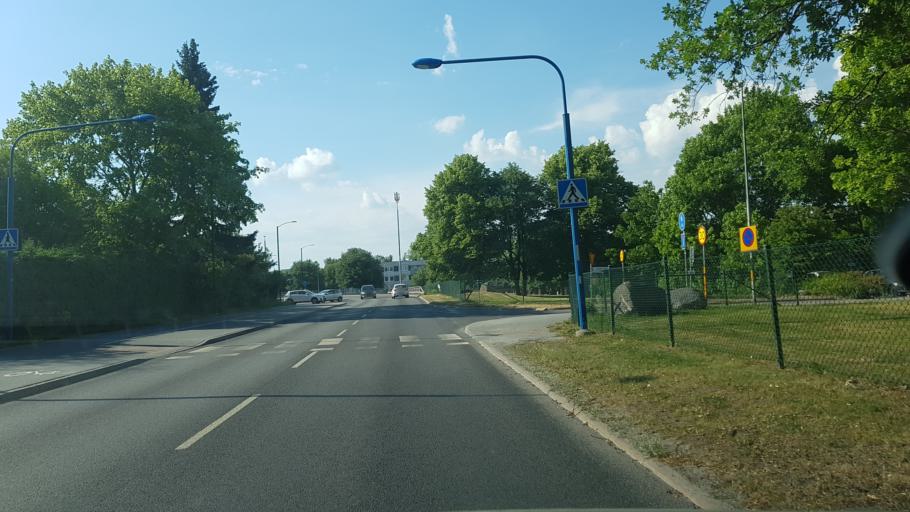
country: SE
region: Stockholm
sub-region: Sollentuna Kommun
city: Sollentuna
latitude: 59.4261
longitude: 17.9413
